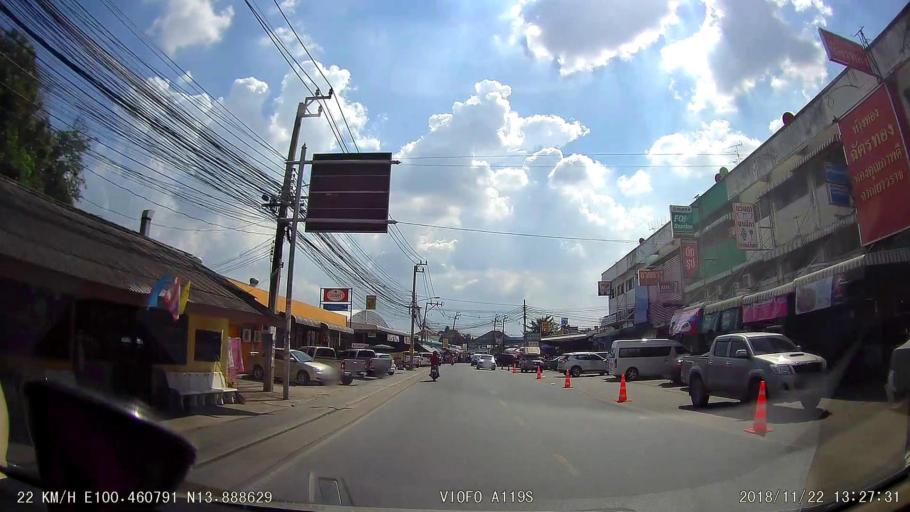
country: TH
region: Nonthaburi
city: Bang Bua Thong
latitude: 13.8887
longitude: 100.4608
